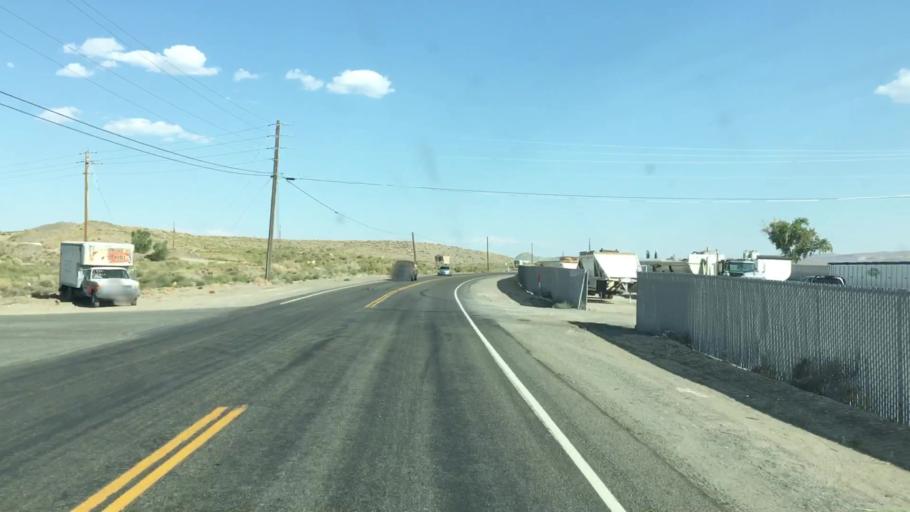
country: US
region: Nevada
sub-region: Lyon County
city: Fernley
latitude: 39.6303
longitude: -119.2780
